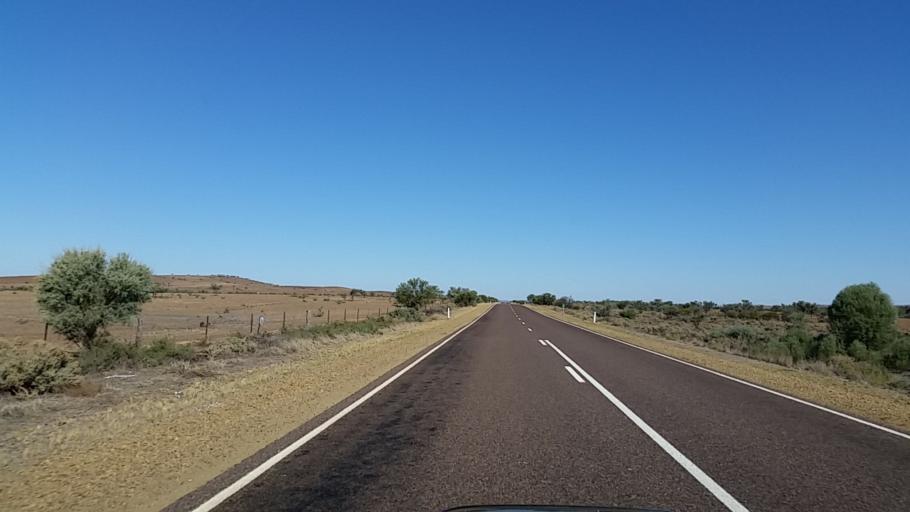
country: AU
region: South Australia
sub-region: Flinders Ranges
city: Quorn
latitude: -32.3433
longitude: 138.4844
